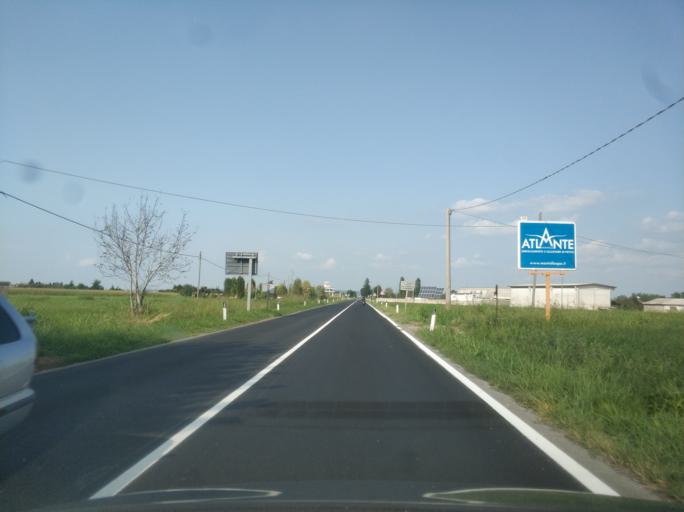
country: IT
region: Piedmont
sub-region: Provincia di Cuneo
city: Cervere
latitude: 44.6409
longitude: 7.7937
